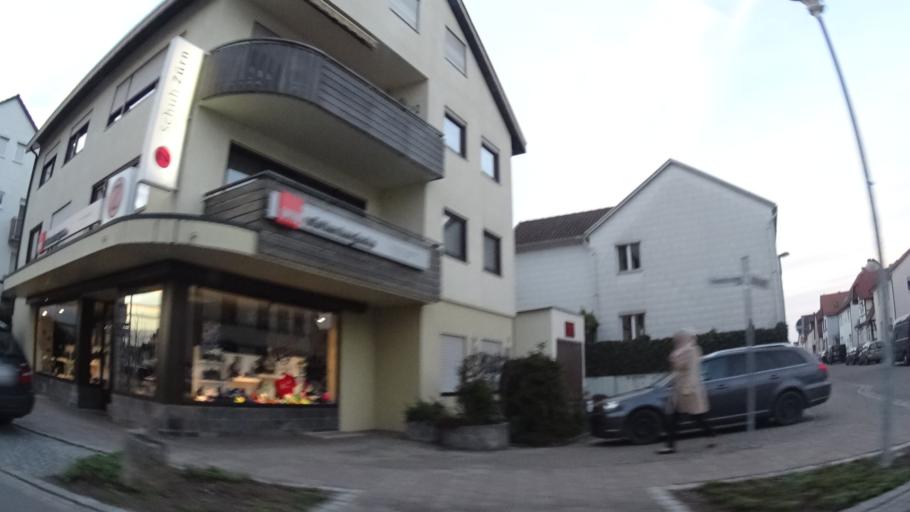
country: DE
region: Baden-Wuerttemberg
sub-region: Regierungsbezirk Stuttgart
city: Tamm
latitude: 48.9207
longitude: 9.1200
